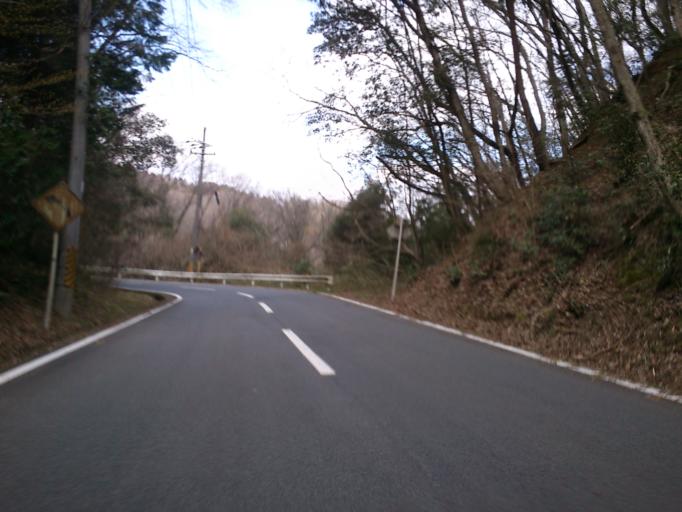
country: JP
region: Mie
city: Ueno-ebisumachi
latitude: 34.7364
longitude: 136.0005
